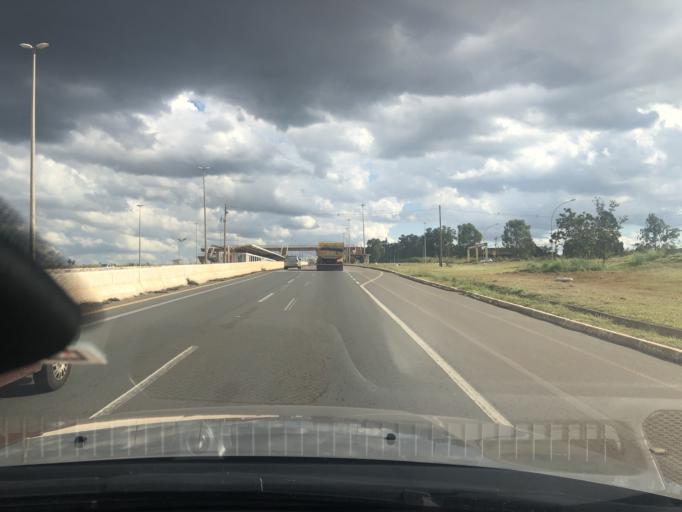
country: BR
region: Federal District
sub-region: Brasilia
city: Brasilia
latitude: -15.9533
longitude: -48.0067
